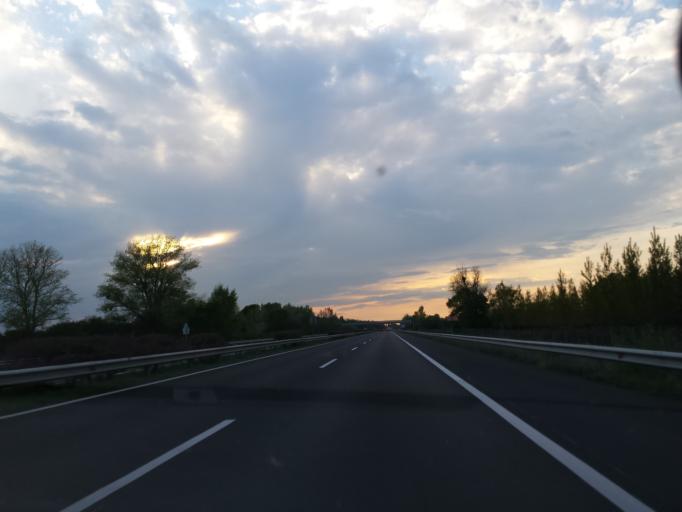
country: HU
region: Gyor-Moson-Sopron
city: Kimle
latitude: 47.7856
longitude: 17.3380
